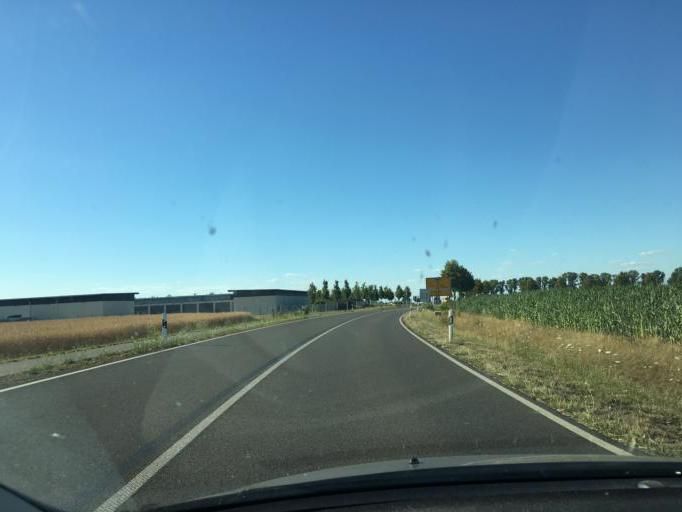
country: DE
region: Saxony
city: Grossposna
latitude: 51.2568
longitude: 12.4679
